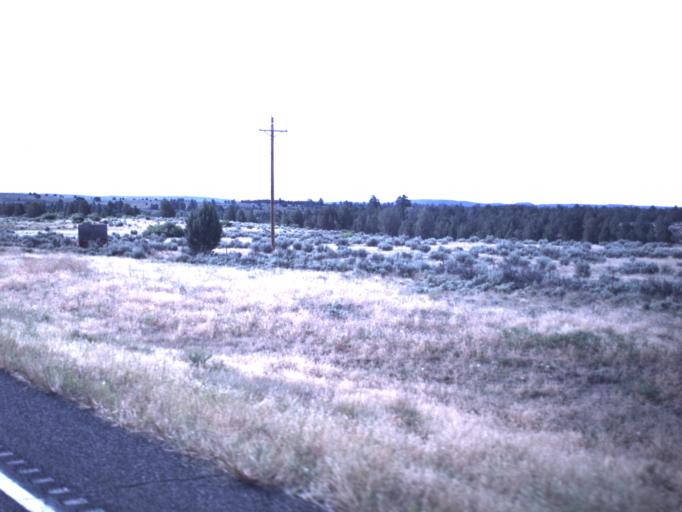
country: US
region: Utah
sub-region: Kane County
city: Kanab
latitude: 37.2362
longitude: -112.7428
